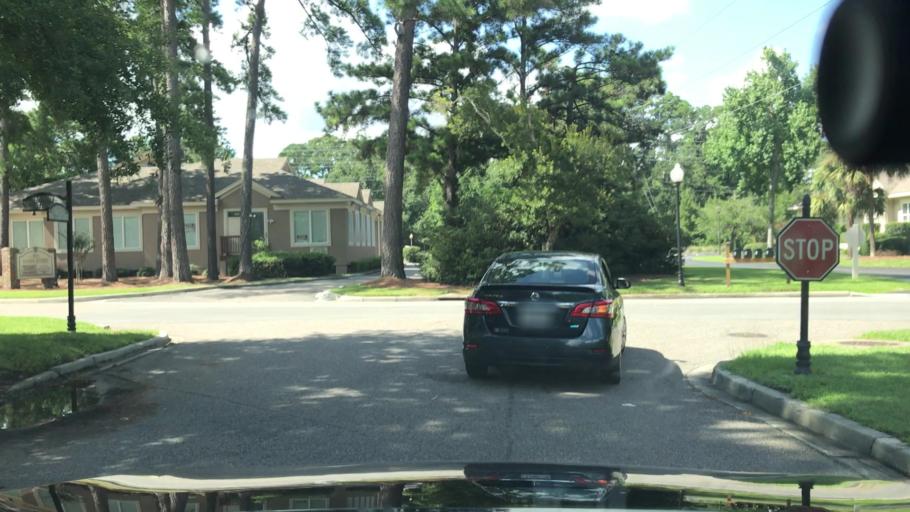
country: US
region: South Carolina
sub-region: Beaufort County
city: Hilton Head Island
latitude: 32.2156
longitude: -80.7302
